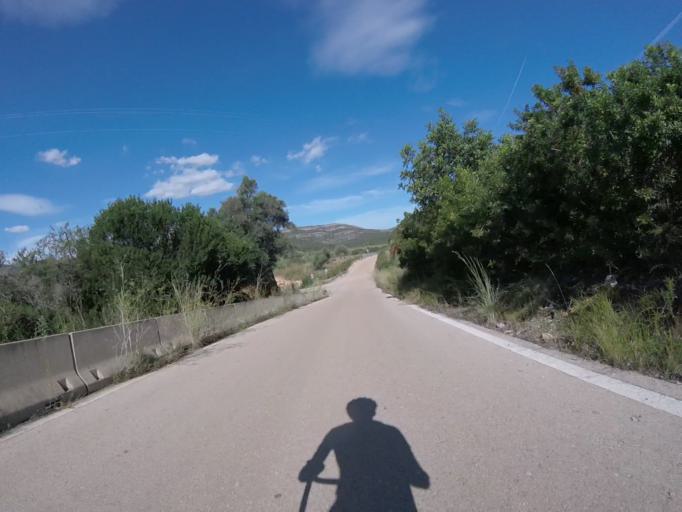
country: ES
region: Valencia
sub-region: Provincia de Castello
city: Santa Magdalena de Pulpis
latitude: 40.3721
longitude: 0.3275
